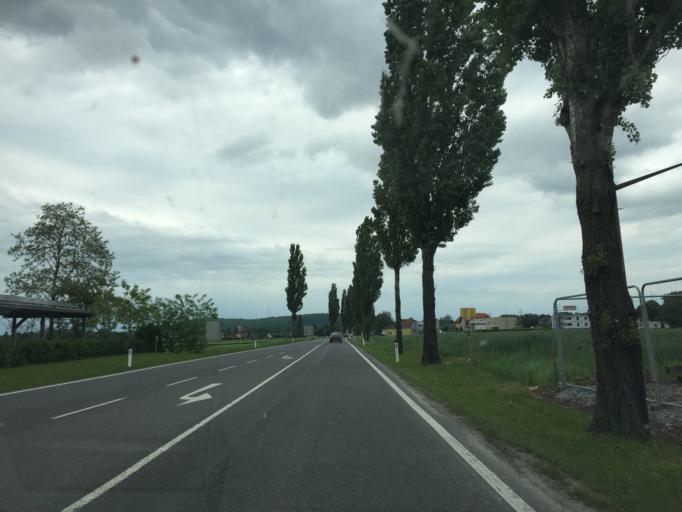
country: AT
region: Lower Austria
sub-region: Politischer Bezirk Sankt Polten
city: Herzogenburg
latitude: 48.2318
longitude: 15.6837
